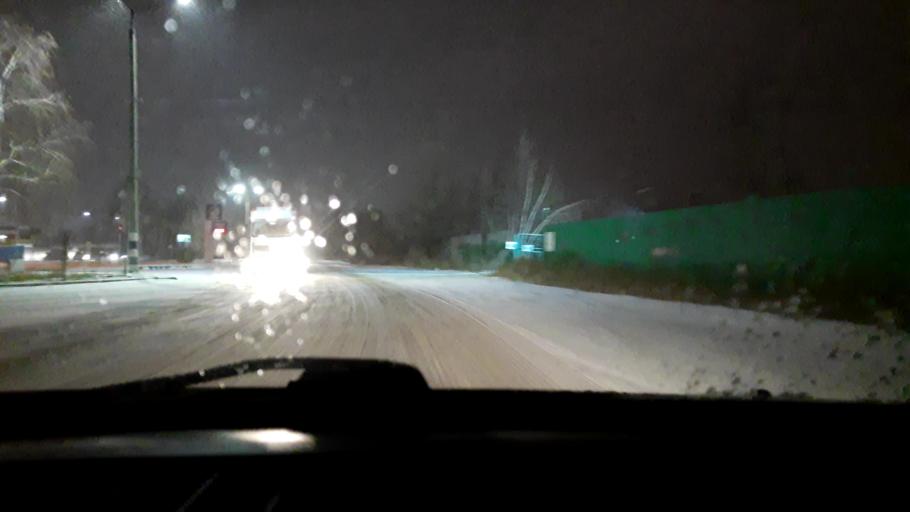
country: RU
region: Nizjnij Novgorod
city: Bor
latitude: 56.3429
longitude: 44.0954
